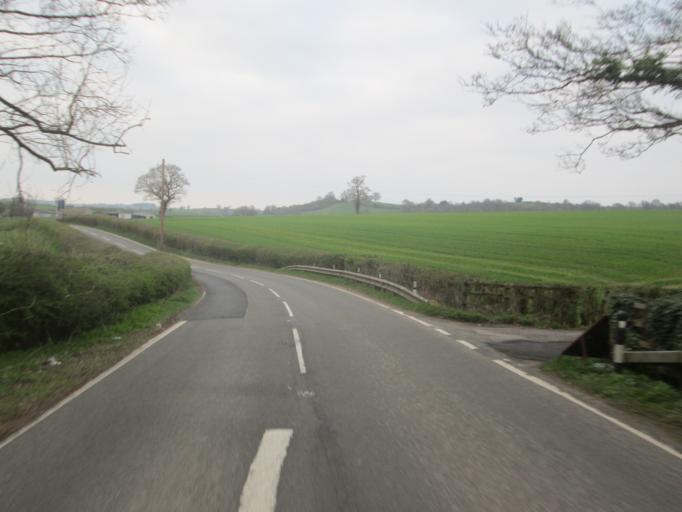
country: GB
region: England
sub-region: Derbyshire
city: Duffield
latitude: 53.0075
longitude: -1.5348
